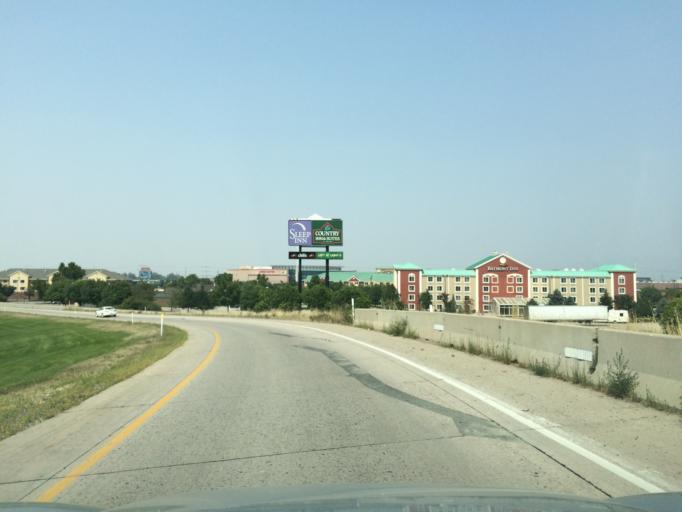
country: US
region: Utah
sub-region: Salt Lake County
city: Taylorsville
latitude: 40.6973
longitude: -111.9497
